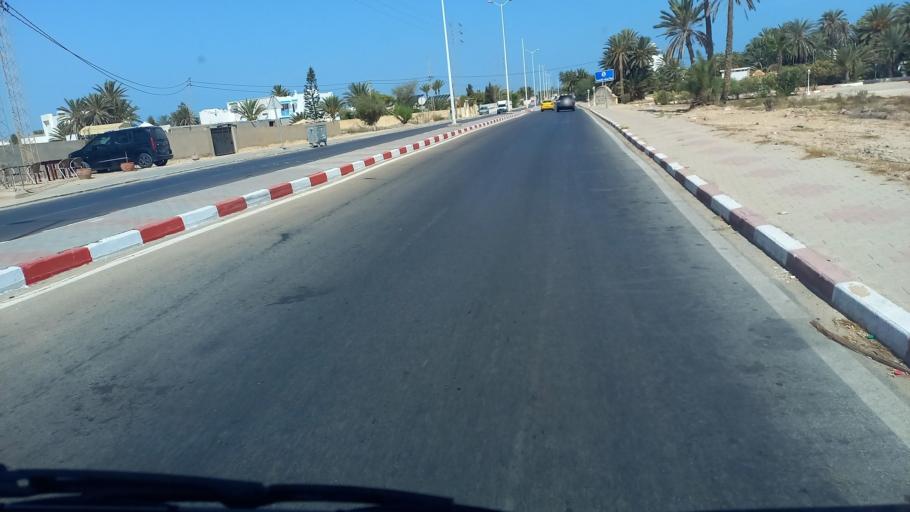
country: TN
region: Madanin
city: Midoun
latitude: 33.8644
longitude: 10.9621
